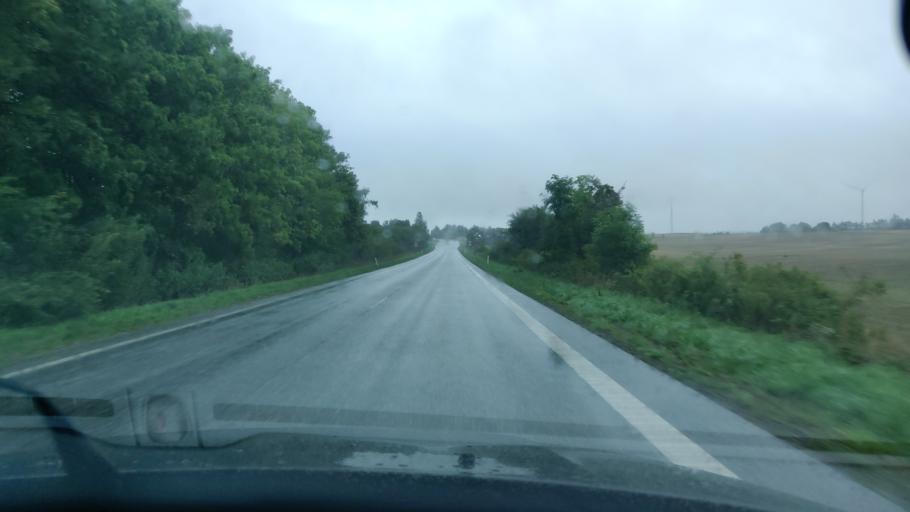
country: DK
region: North Denmark
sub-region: Thisted Kommune
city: Hurup
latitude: 56.8430
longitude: 8.5261
